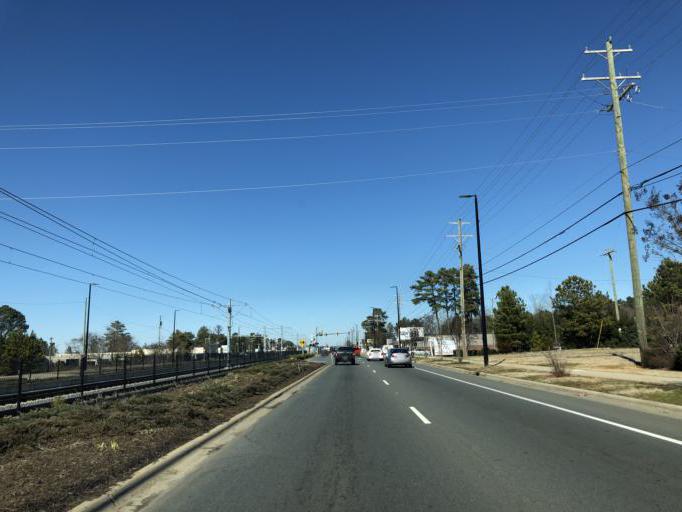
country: US
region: North Carolina
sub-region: Mecklenburg County
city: Charlotte
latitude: 35.2733
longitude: -80.7671
